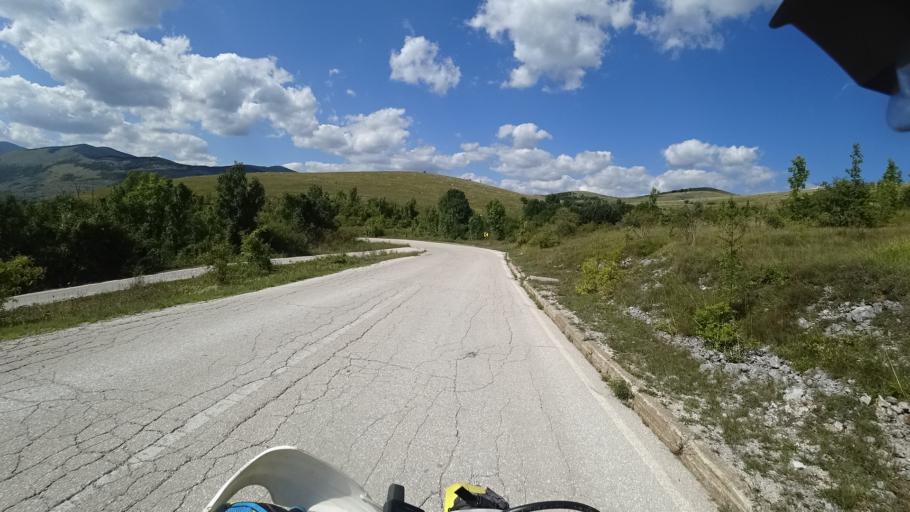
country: BA
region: Federation of Bosnia and Herzegovina
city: Orasac
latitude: 44.4659
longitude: 15.9795
